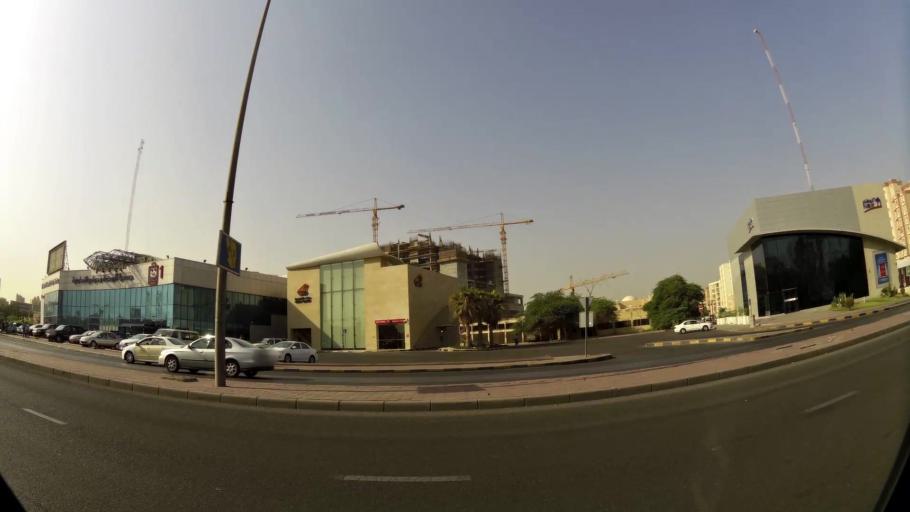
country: KW
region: Muhafazat Hawalli
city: Hawalli
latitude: 29.3401
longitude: 48.0213
